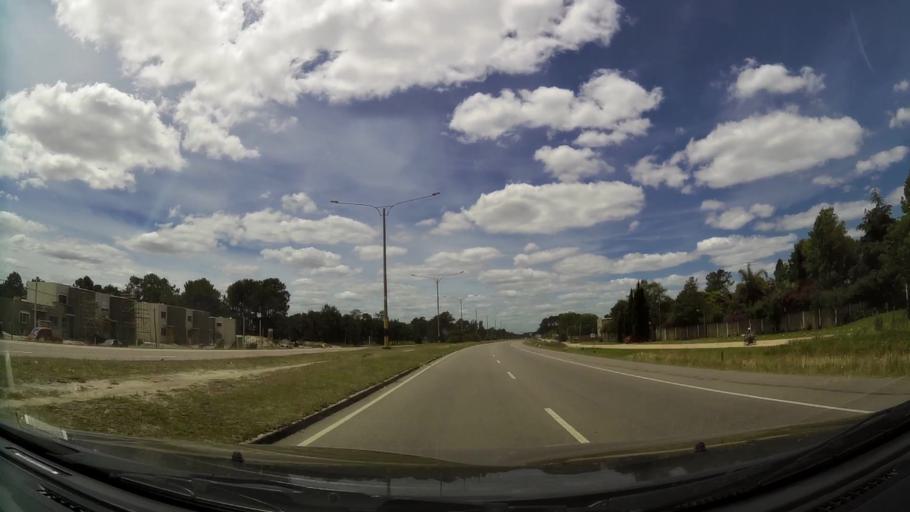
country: UY
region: Canelones
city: Pando
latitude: -34.7985
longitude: -55.9160
